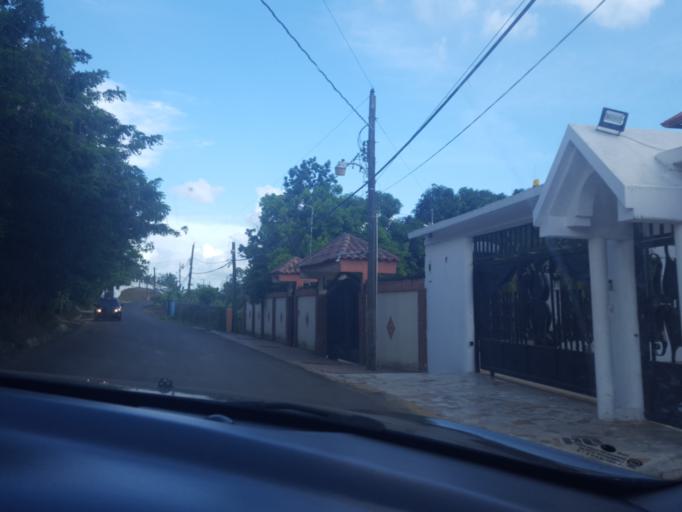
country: DO
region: La Vega
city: Rio Verde Arriba
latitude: 19.3533
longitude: -70.6294
